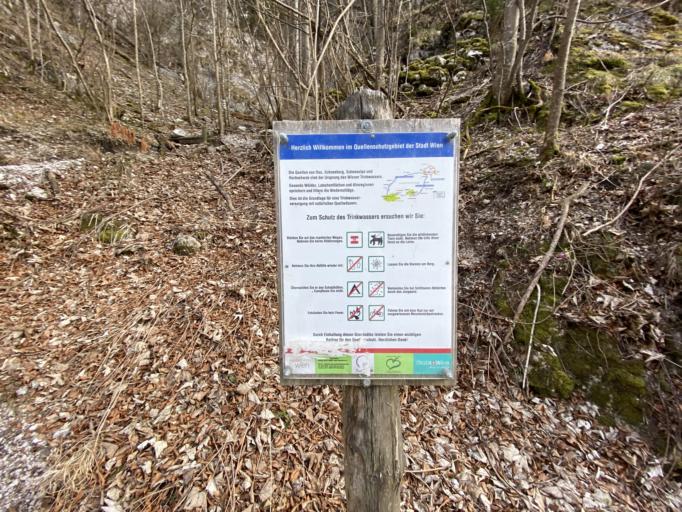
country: AT
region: Lower Austria
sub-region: Politischer Bezirk Neunkirchen
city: Schwarzau im Gebirge
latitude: 47.7465
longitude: 15.7638
